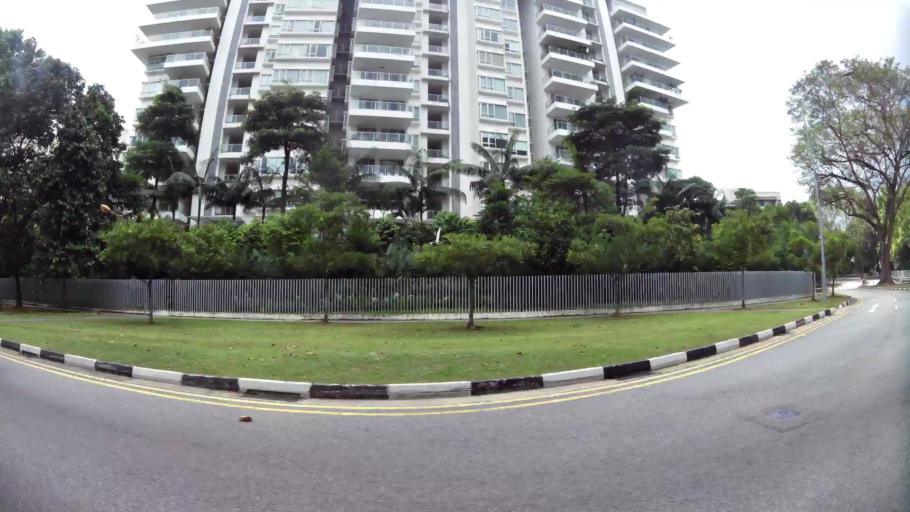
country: SG
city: Singapore
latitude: 1.3142
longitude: 103.8267
